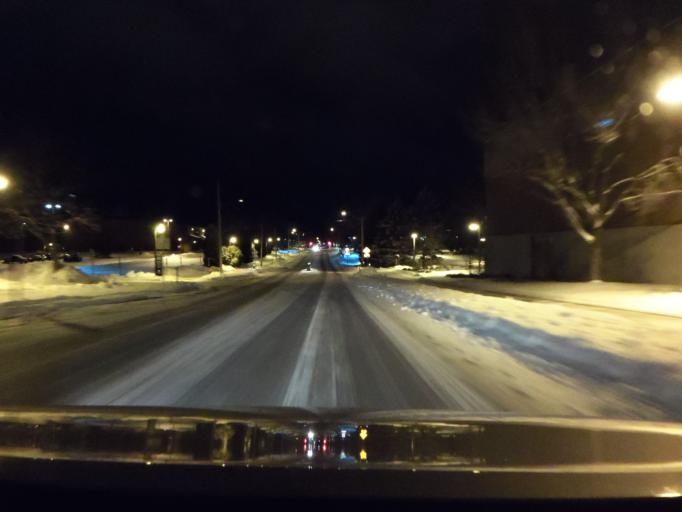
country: US
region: Wisconsin
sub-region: Dunn County
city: Menomonie
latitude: 44.8711
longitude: -91.9251
